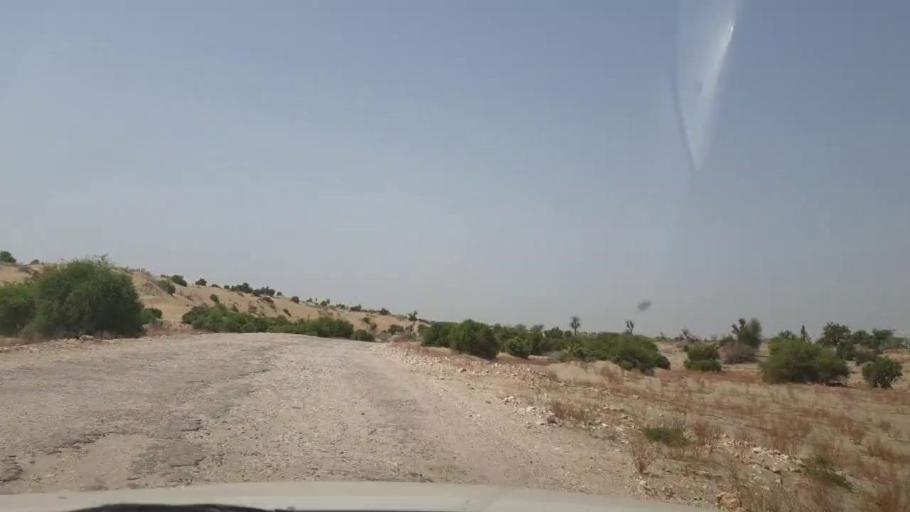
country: PK
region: Sindh
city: Khanpur
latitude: 27.3688
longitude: 69.3178
